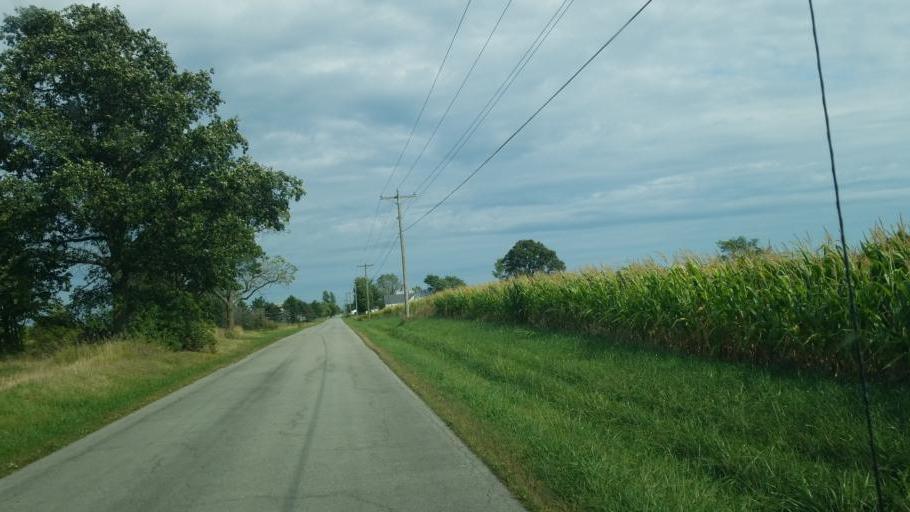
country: US
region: Ohio
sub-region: Hancock County
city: Arlington
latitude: 40.8773
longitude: -83.6264
